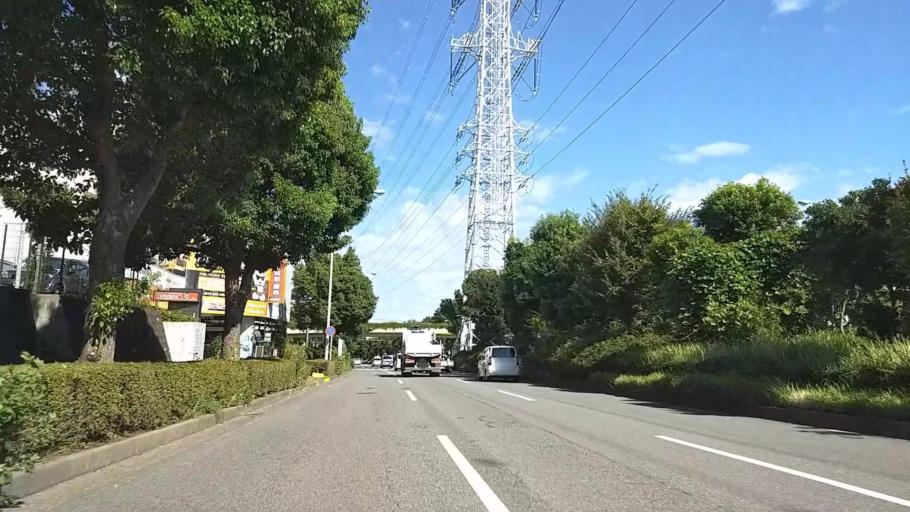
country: JP
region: Tokyo
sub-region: Machida-shi
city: Machida
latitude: 35.5421
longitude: 139.5615
